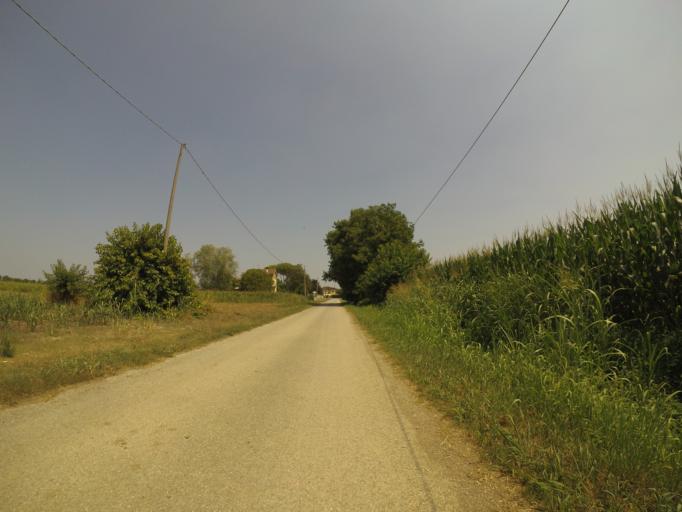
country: IT
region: Friuli Venezia Giulia
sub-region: Provincia di Udine
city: Talmassons
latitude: 45.9187
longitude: 13.1338
